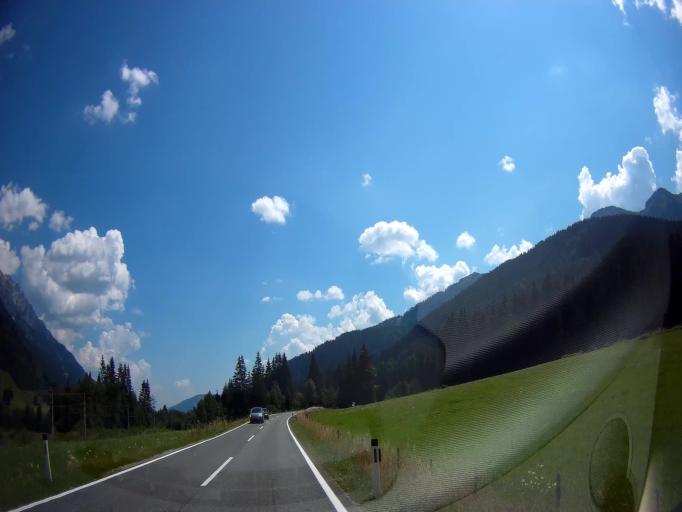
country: AT
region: Tyrol
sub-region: Politischer Bezirk Kitzbuhel
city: Hochfilzen
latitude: 47.4579
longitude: 12.6407
